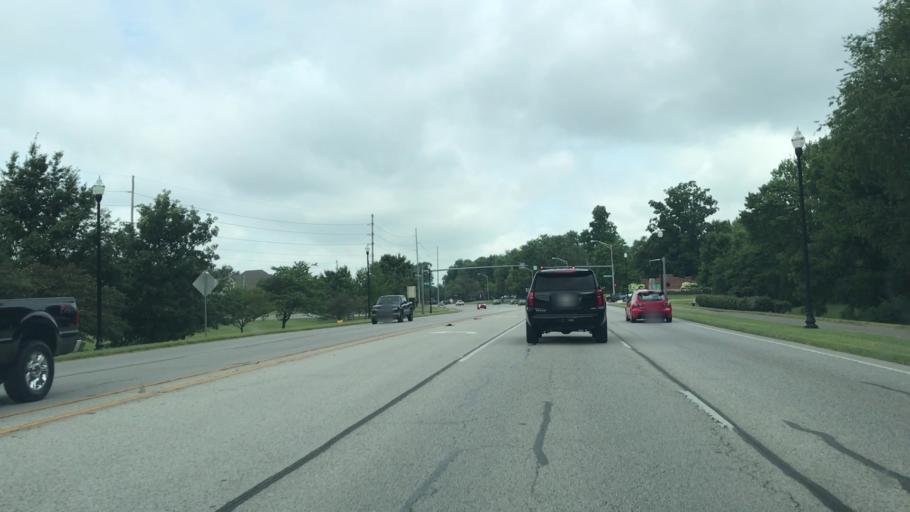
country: US
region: Kentucky
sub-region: Warren County
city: Bowling Green
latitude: 36.9870
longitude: -86.4031
